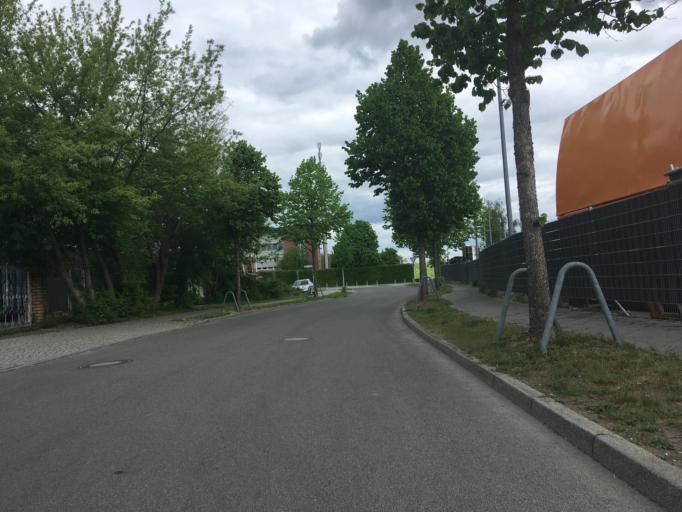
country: DE
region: Berlin
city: Neu-Hohenschoenhausen
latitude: 52.5554
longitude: 13.5297
